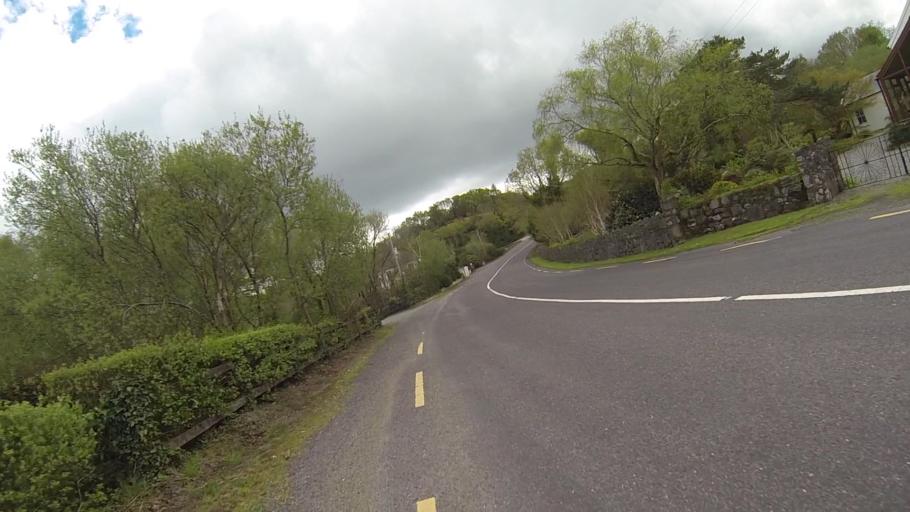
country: IE
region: Munster
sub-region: County Cork
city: Bantry
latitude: 51.7344
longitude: -9.5592
